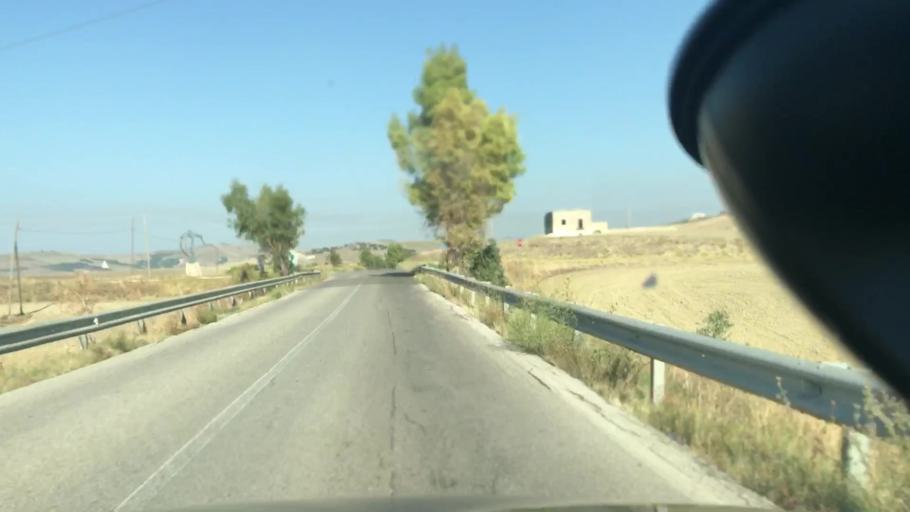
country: IT
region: Basilicate
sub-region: Provincia di Matera
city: La Martella
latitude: 40.6674
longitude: 16.4883
